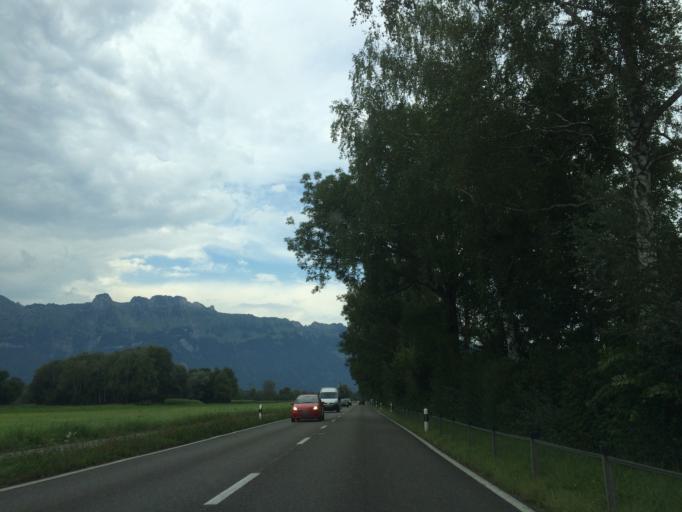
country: LI
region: Schaan
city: Schaan
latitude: 47.1882
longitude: 9.5047
